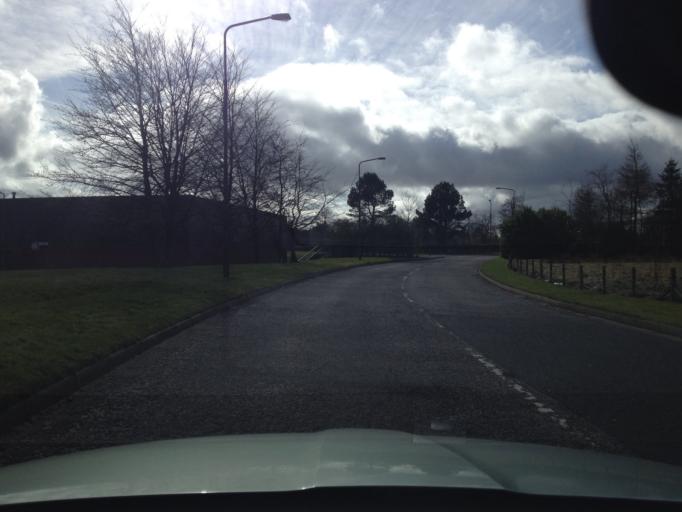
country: GB
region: Scotland
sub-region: West Lothian
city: Livingston
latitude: 55.8671
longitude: -3.5320
